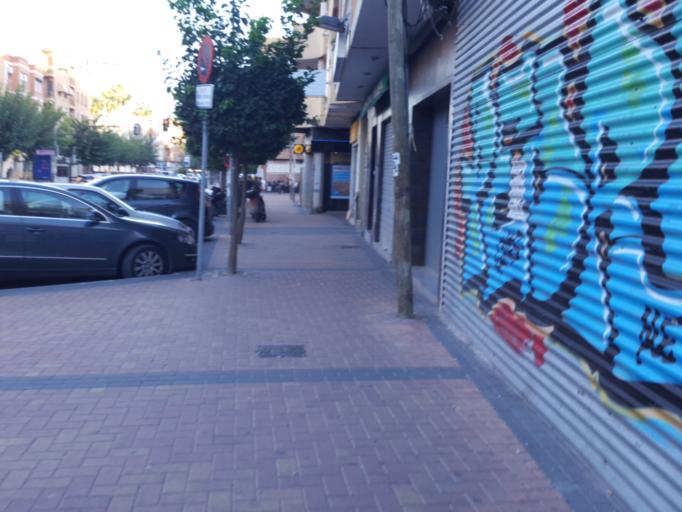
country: ES
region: Murcia
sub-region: Murcia
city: Murcia
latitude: 38.0090
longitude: -1.1522
